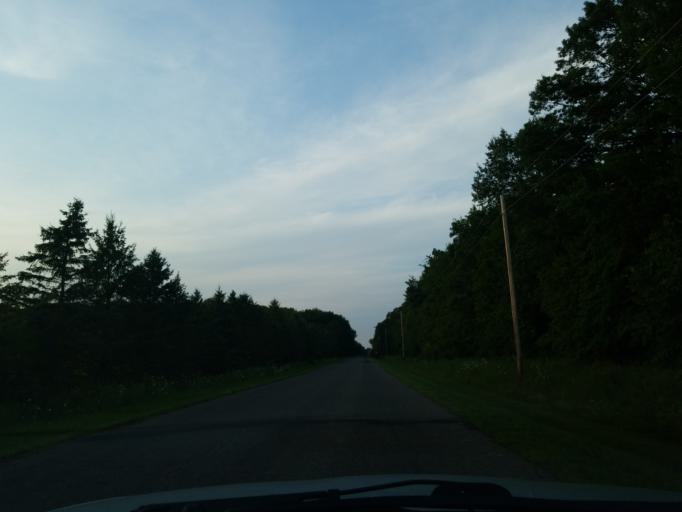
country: US
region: Minnesota
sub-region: Washington County
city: Stillwater
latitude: 45.0758
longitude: -92.7713
